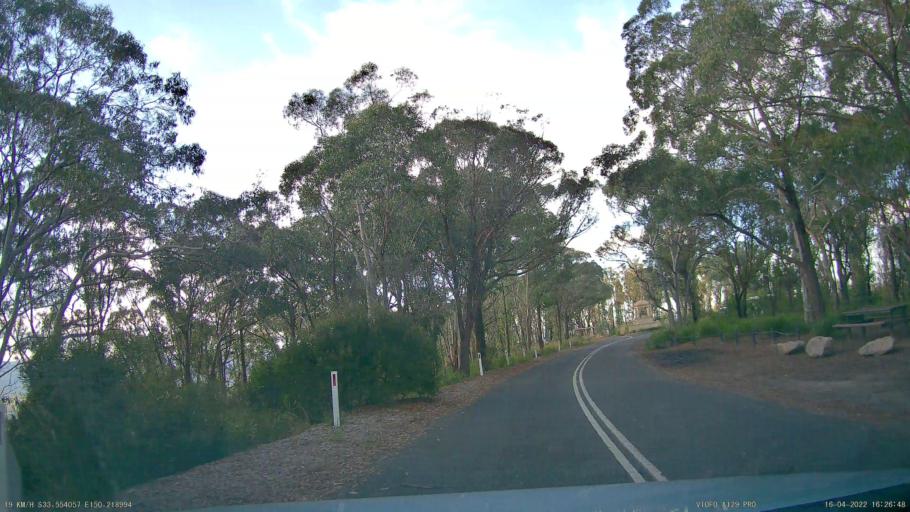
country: AU
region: New South Wales
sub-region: Blue Mountains Municipality
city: Blackheath
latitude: -33.5540
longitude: 150.2190
